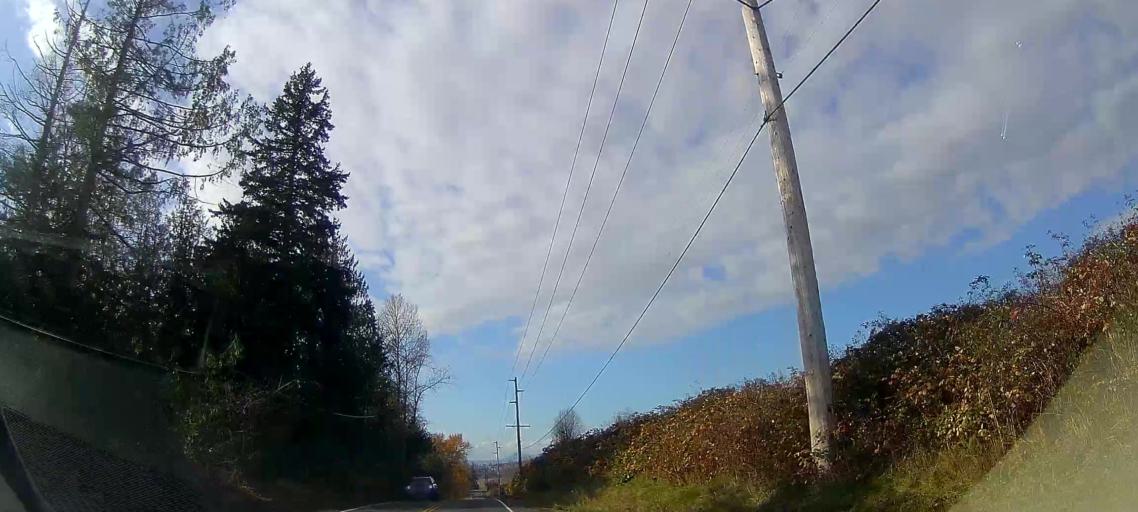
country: US
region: Washington
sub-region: Skagit County
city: Big Lake
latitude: 48.4353
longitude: -122.2564
